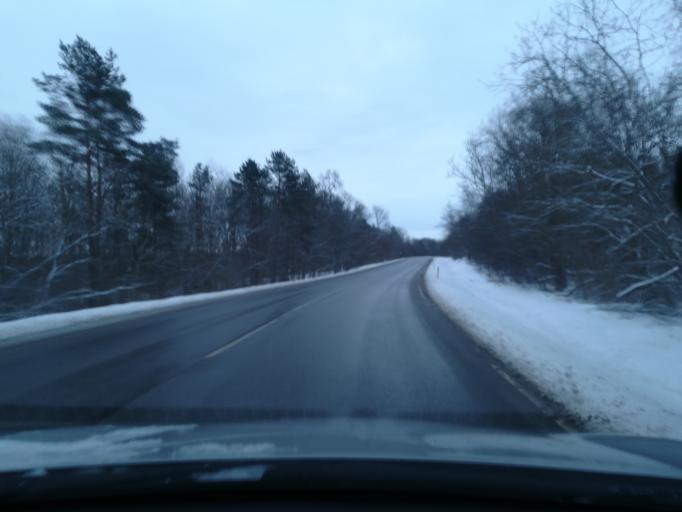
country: EE
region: Harju
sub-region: Keila linn
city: Keila
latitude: 59.4214
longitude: 24.3332
